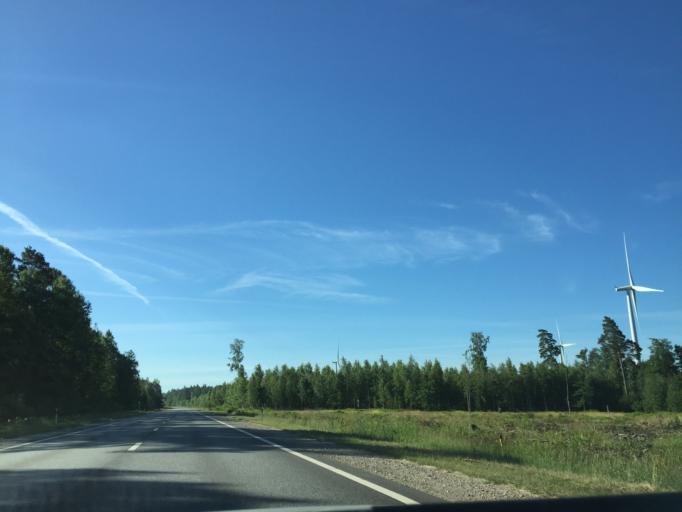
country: LV
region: Ventspils
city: Ventspils
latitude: 57.3858
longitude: 21.7068
